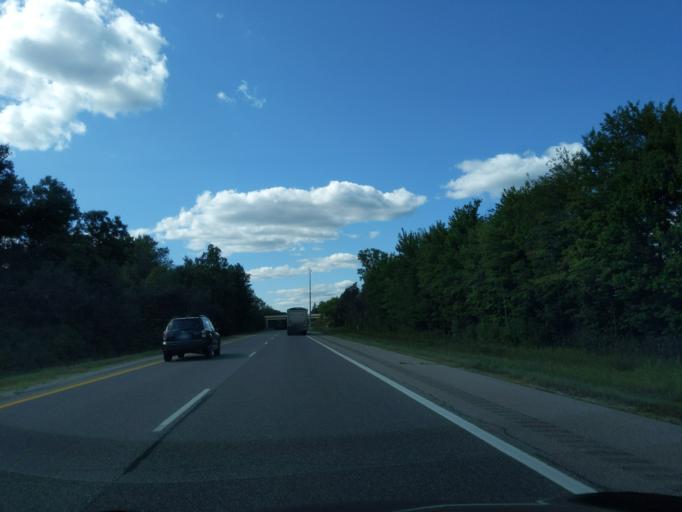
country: US
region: Michigan
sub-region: Muskegon County
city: Fruitport
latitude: 43.1193
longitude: -86.1306
